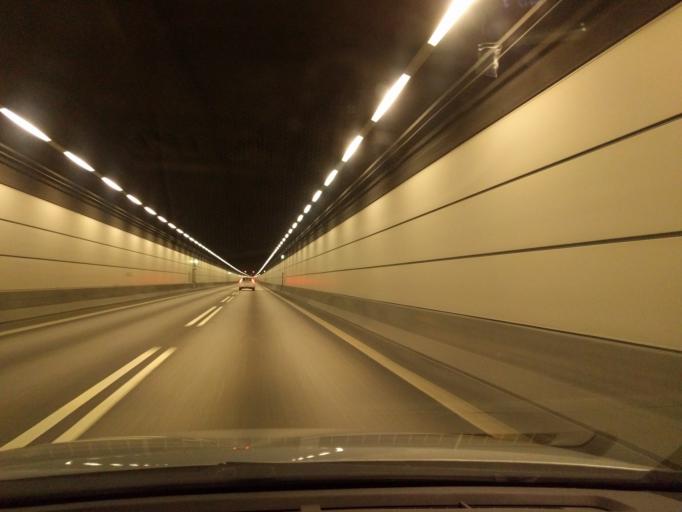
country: DK
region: Capital Region
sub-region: Dragor Kommune
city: Dragor
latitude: 55.6278
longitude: 12.6855
